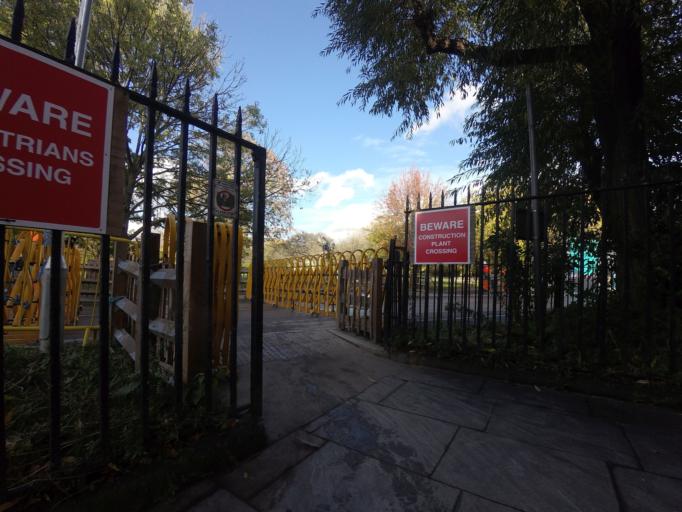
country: GB
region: England
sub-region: Greater London
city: Bethnal Green
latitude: 51.5086
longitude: -0.0485
